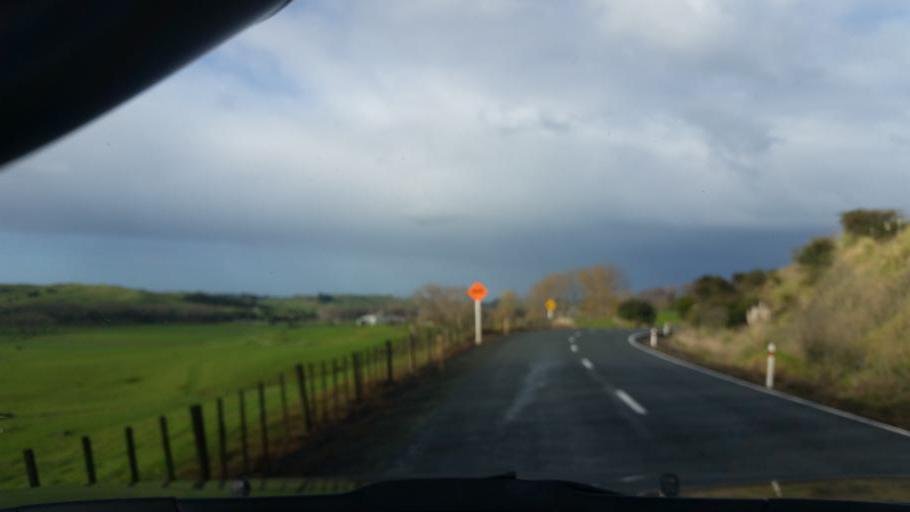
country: NZ
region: Northland
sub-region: Kaipara District
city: Dargaville
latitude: -35.8315
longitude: 173.9278
